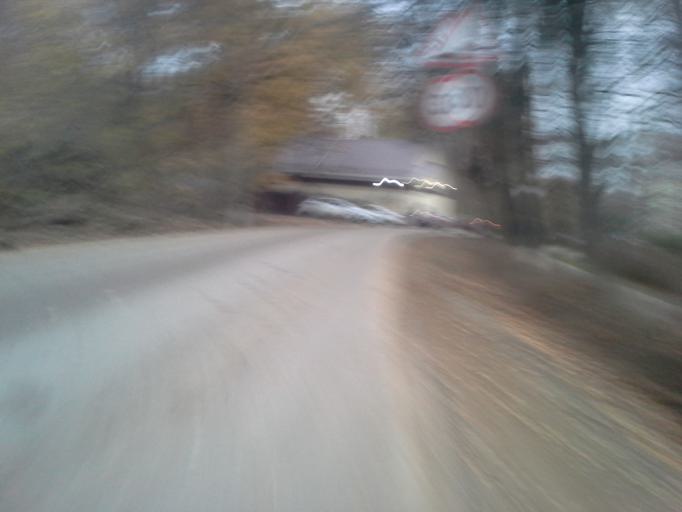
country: RU
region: Moskovskaya
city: Kommunarka
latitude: 55.5617
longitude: 37.4766
